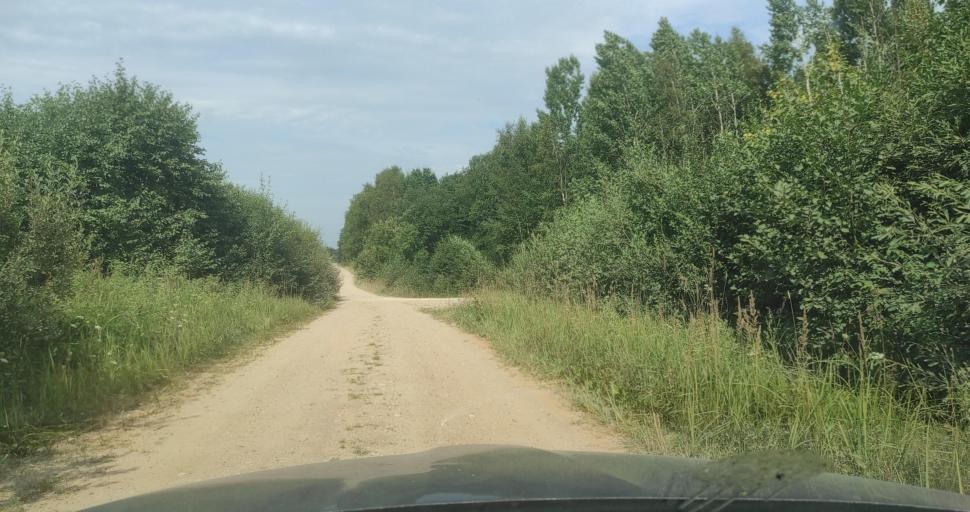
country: LV
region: Kuldigas Rajons
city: Kuldiga
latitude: 56.9809
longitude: 22.0716
